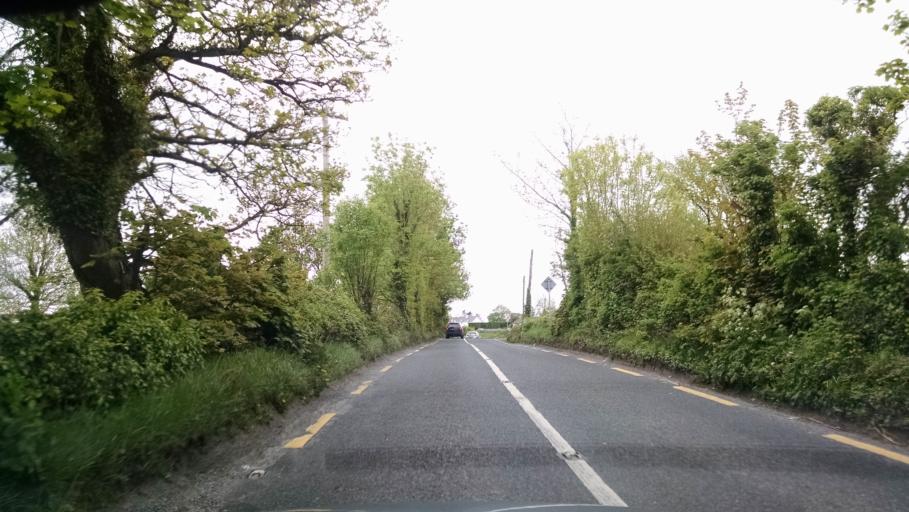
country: IE
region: Connaught
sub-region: County Galway
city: Claregalway
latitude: 53.4318
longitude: -9.0566
